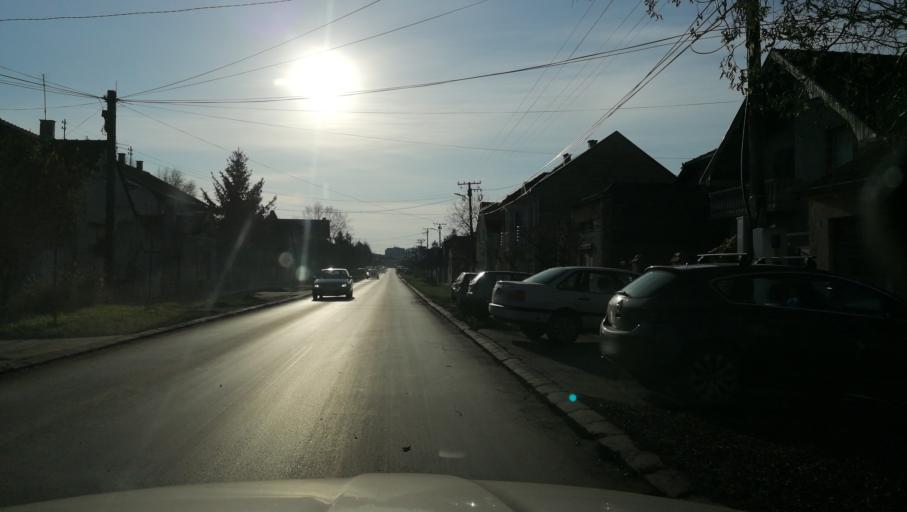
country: RS
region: Autonomna Pokrajina Vojvodina
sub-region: Sremski Okrug
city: Sremska Mitrovica
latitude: 44.9704
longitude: 19.6186
